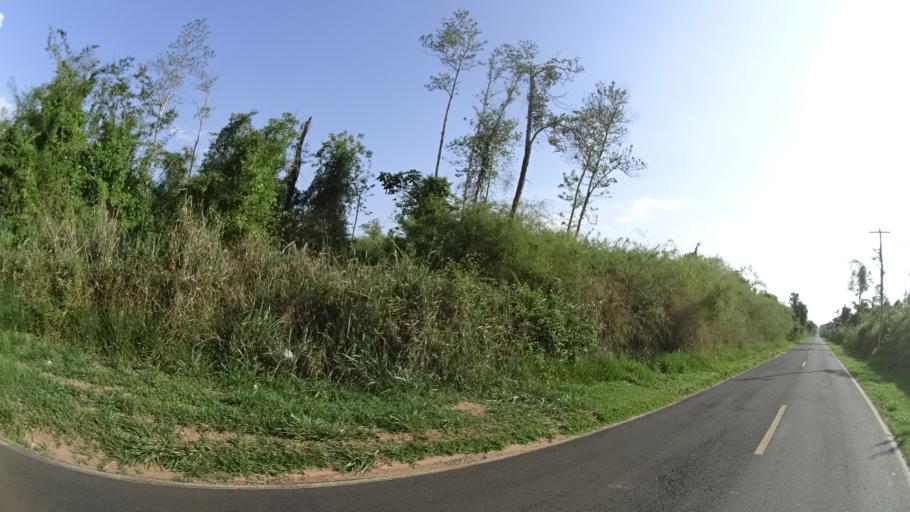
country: BR
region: Sao Paulo
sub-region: Urupes
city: Urupes
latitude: -21.3759
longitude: -49.4799
